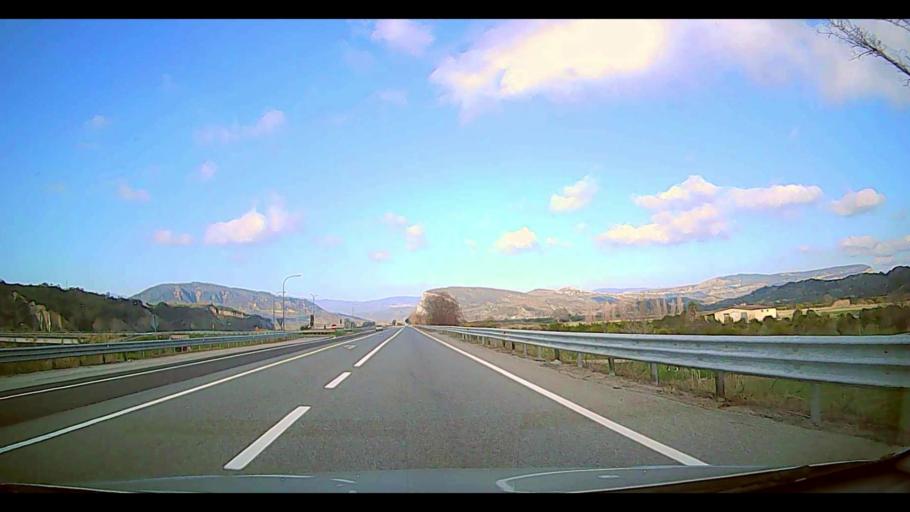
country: IT
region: Calabria
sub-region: Provincia di Crotone
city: Santa Severina
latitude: 39.1751
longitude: 16.9340
